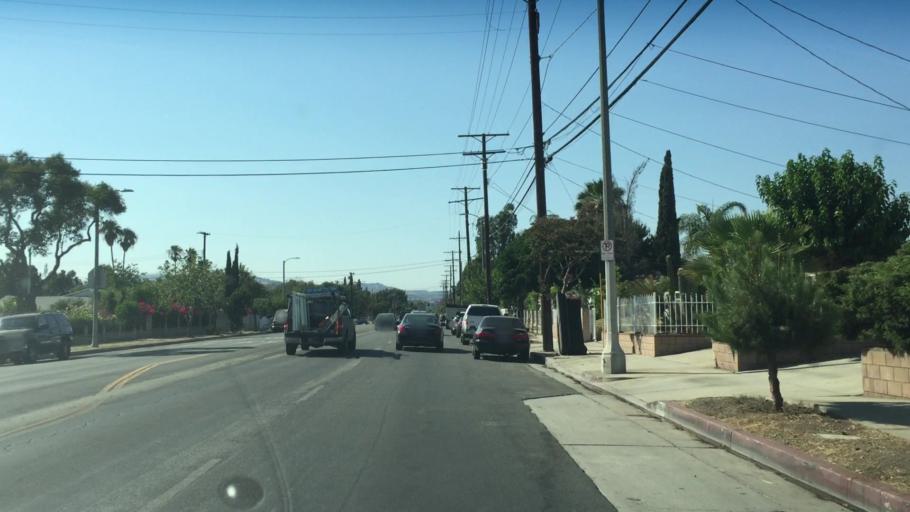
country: US
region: California
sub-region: Los Angeles County
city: San Fernando
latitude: 34.2513
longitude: -118.4357
